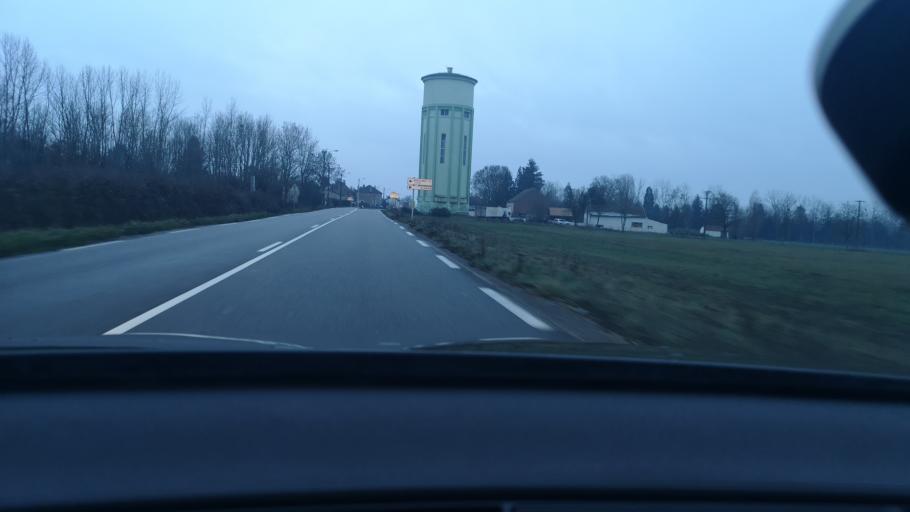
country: FR
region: Bourgogne
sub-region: Departement de la Cote-d'Or
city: Seurre
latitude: 47.0683
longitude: 5.0987
